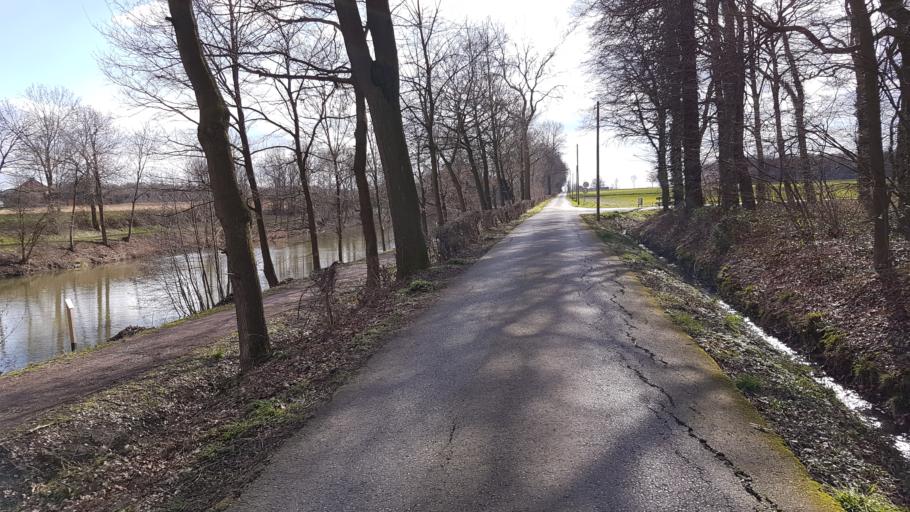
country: DE
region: North Rhine-Westphalia
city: Olfen
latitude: 51.6952
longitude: 7.3780
